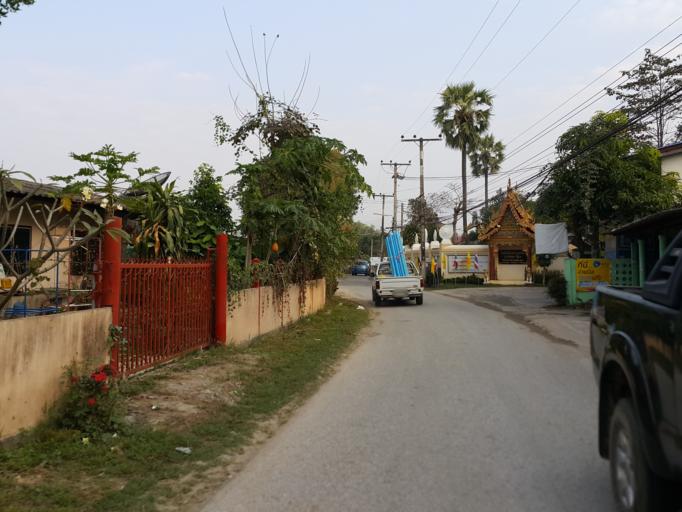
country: TH
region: Chiang Mai
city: San Sai
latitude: 18.8155
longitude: 99.0990
